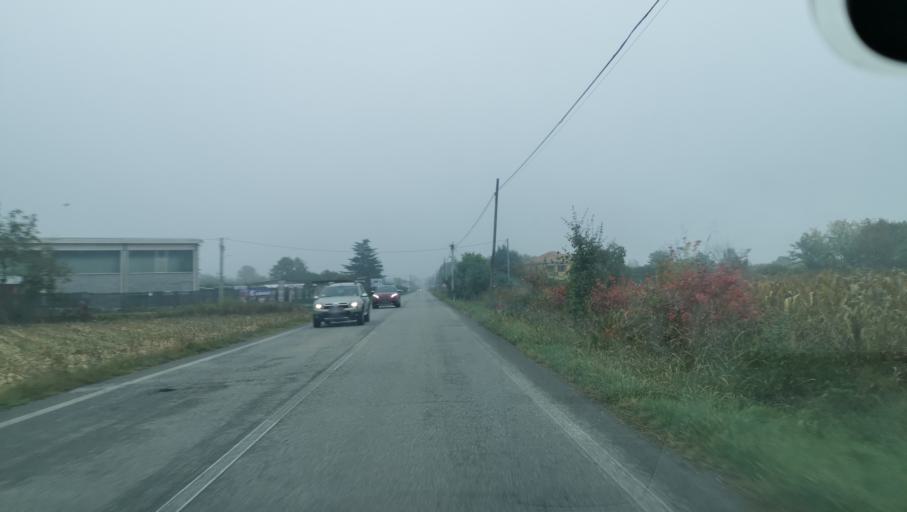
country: IT
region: Piedmont
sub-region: Provincia di Biella
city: Cavaglia
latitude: 45.3916
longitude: 8.0880
